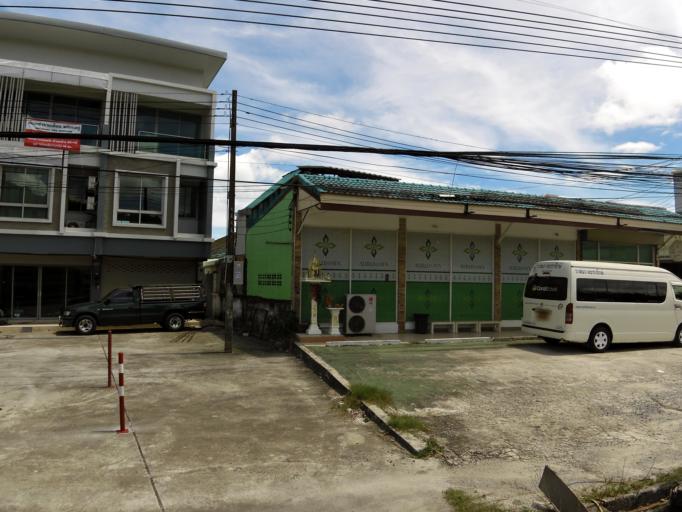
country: TH
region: Phuket
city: Mueang Phuket
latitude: 7.8661
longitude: 98.3496
